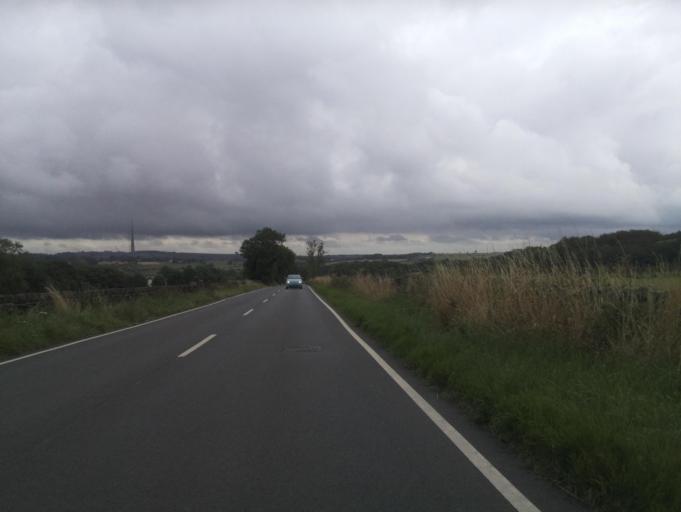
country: GB
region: England
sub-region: Kirklees
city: Shelley
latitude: 53.5812
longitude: -1.6910
